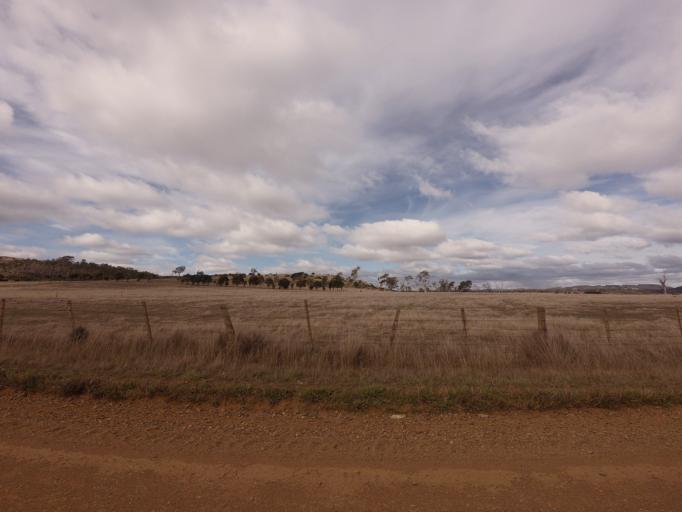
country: AU
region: Tasmania
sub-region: Brighton
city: Bridgewater
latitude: -42.4225
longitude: 147.3913
